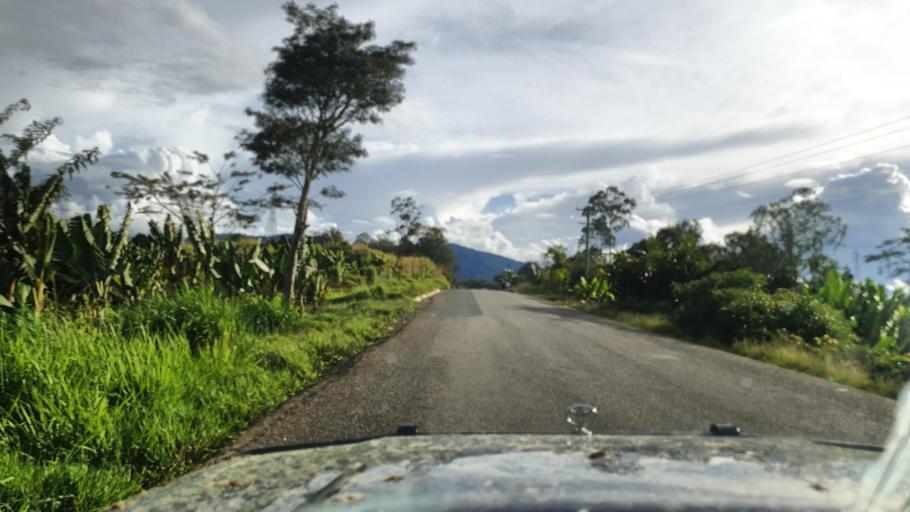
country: PG
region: Jiwaka
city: Minj
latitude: -5.8802
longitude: 144.6892
